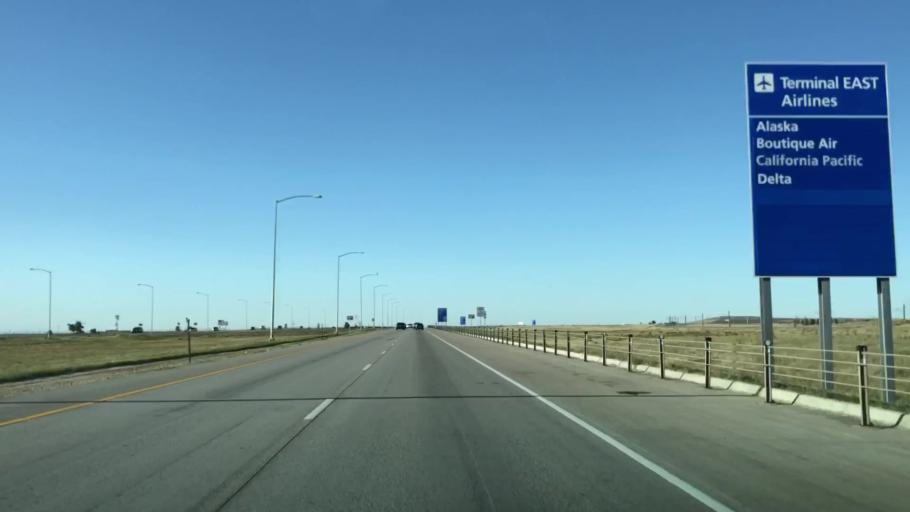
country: US
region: Colorado
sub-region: Adams County
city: Aurora
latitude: 39.8148
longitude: -104.7862
